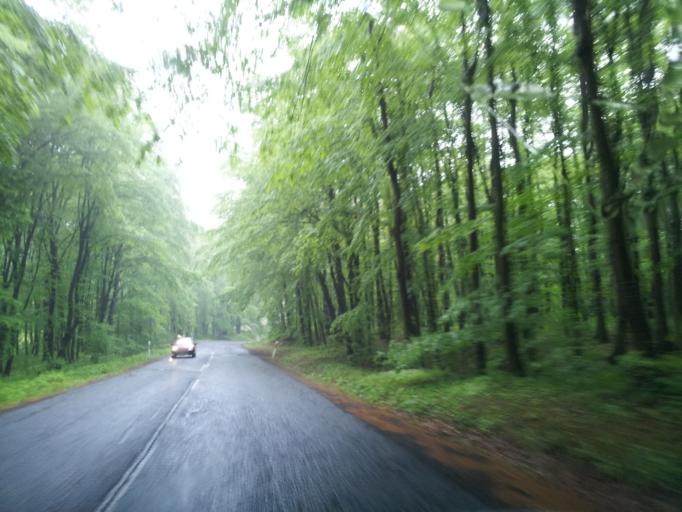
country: HU
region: Baranya
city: Hosszuheteny
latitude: 46.1877
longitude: 18.3204
